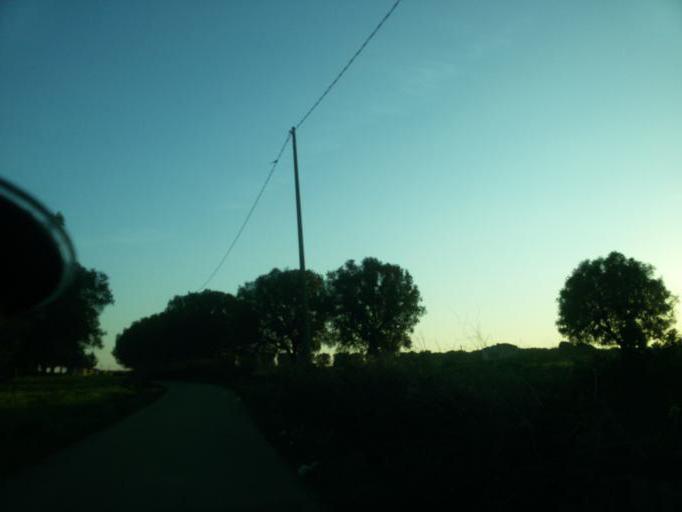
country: IT
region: Apulia
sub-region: Provincia di Brindisi
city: La Rosa
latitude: 40.6120
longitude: 17.9396
